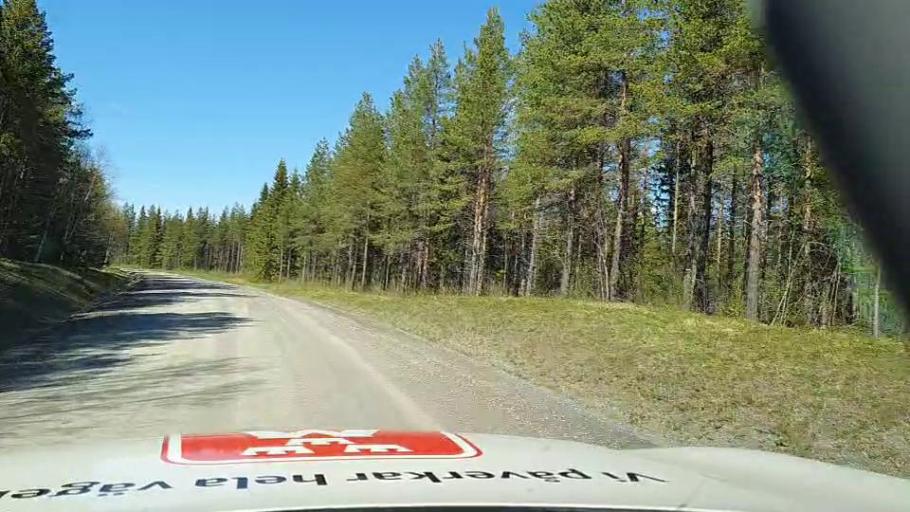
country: SE
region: Jaemtland
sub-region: Krokoms Kommun
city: Valla
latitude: 63.6551
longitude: 13.7772
